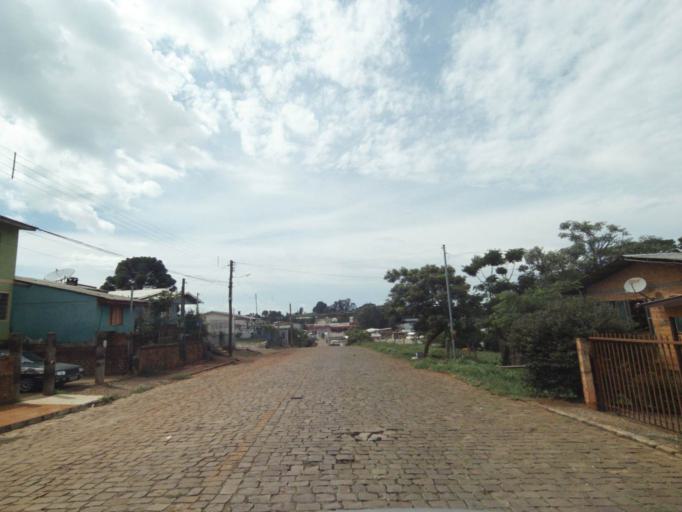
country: BR
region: Rio Grande do Sul
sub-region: Lagoa Vermelha
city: Lagoa Vermelha
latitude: -28.2237
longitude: -51.5144
